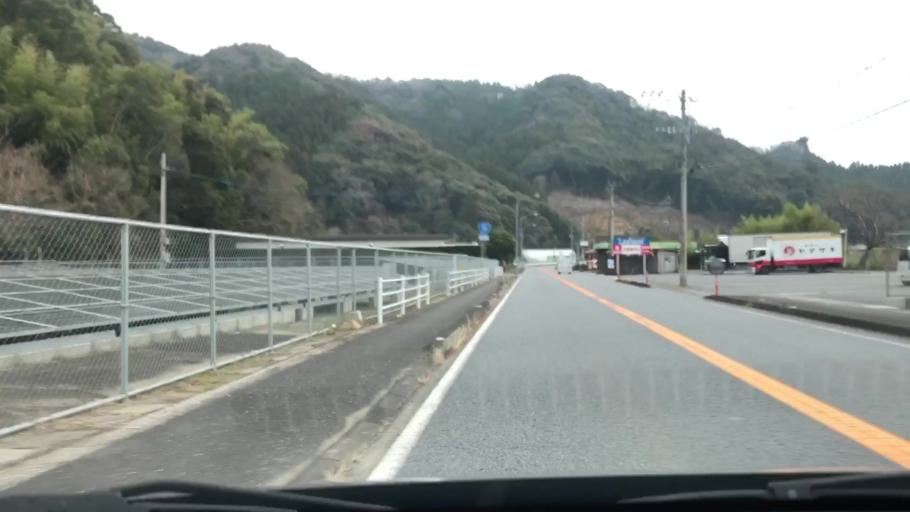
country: JP
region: Oita
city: Saiki
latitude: 32.9860
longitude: 131.8427
